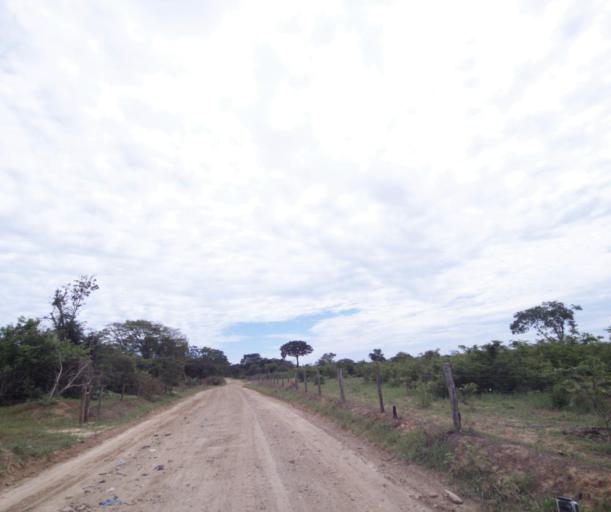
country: BR
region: Bahia
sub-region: Carinhanha
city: Carinhanha
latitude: -14.2281
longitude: -44.3025
